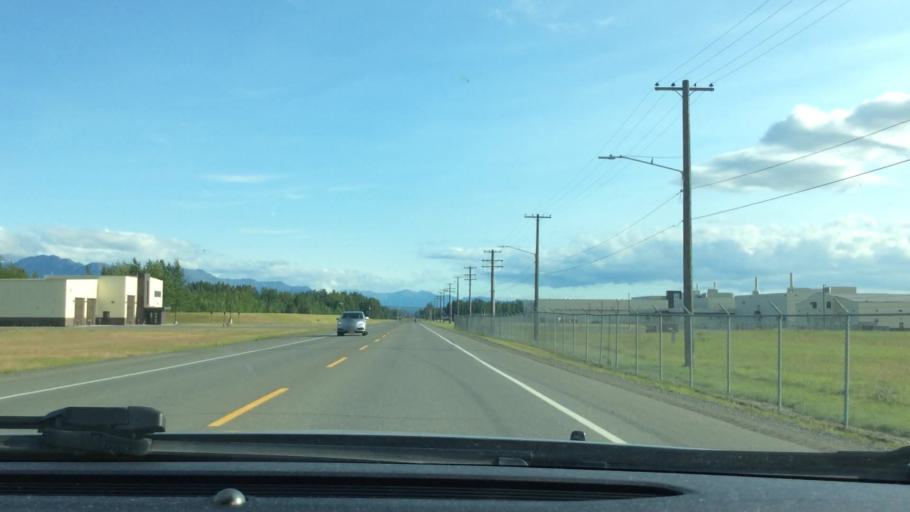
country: US
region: Alaska
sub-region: Anchorage Municipality
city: Anchorage
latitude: 61.2481
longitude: -149.7787
